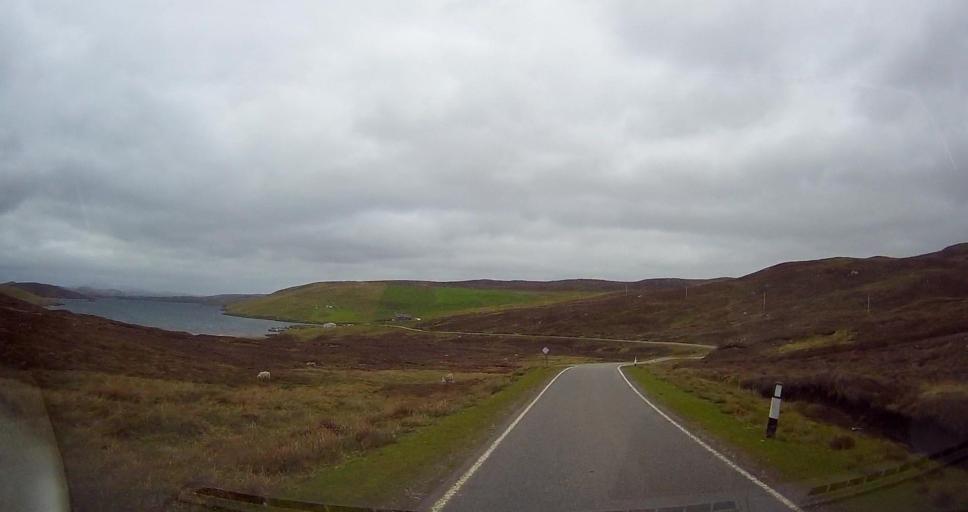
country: GB
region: Scotland
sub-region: Shetland Islands
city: Lerwick
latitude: 60.3288
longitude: -1.3379
